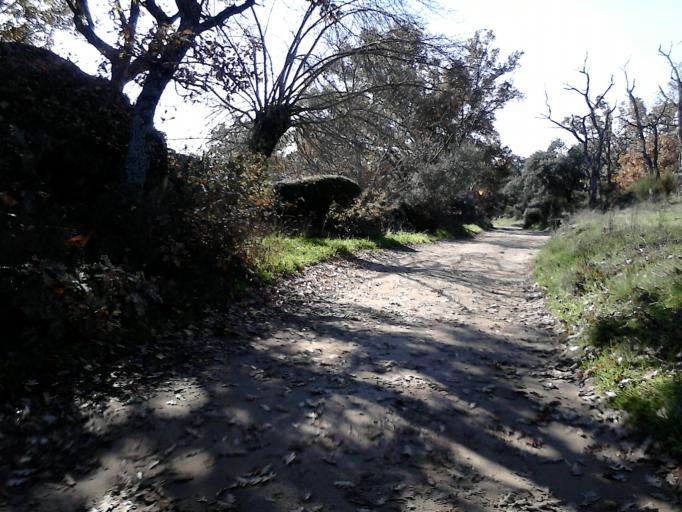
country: ES
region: Madrid
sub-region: Provincia de Madrid
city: El Escorial
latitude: 40.5973
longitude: -4.1088
